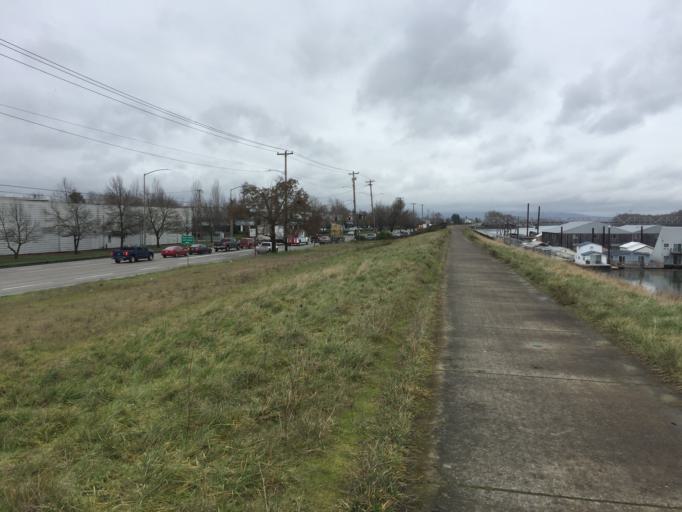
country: US
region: Washington
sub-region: Clark County
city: Vancouver
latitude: 45.6089
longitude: -122.6892
